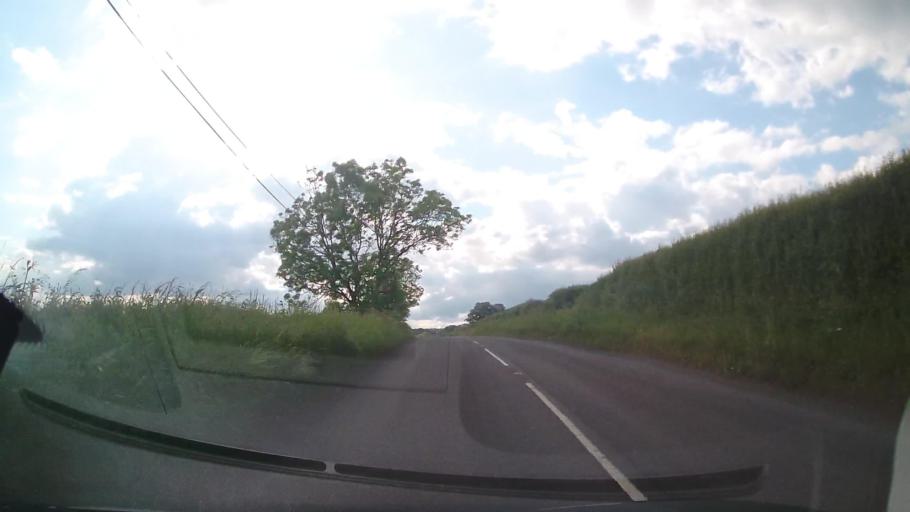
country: GB
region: England
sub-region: Shropshire
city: Harley
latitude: 52.6484
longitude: -2.5824
